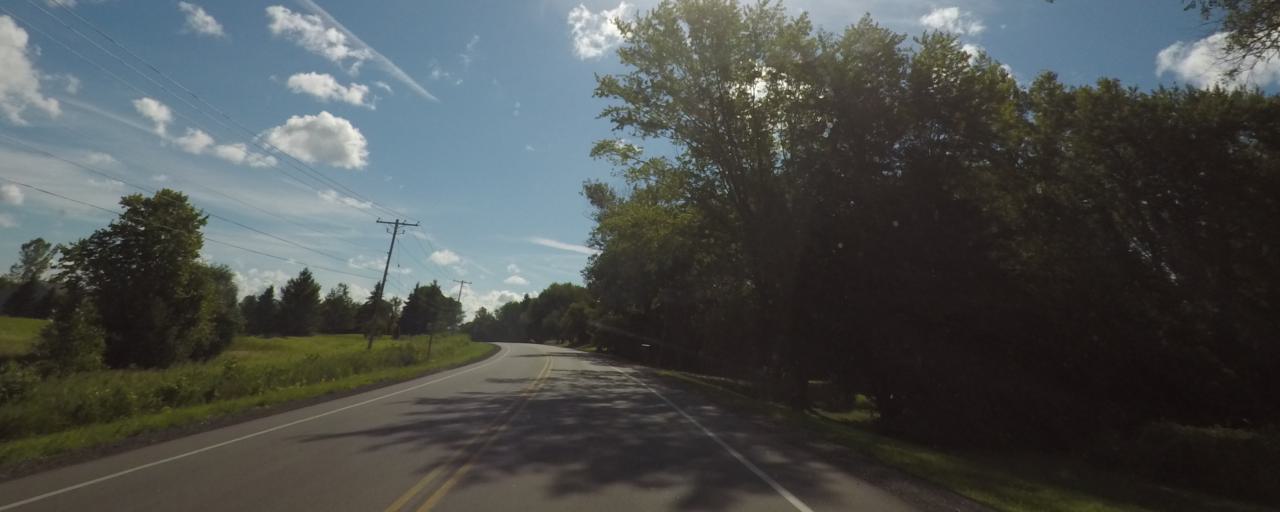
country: US
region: Wisconsin
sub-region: Waukesha County
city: Oconomowoc
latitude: 43.0748
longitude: -88.5541
